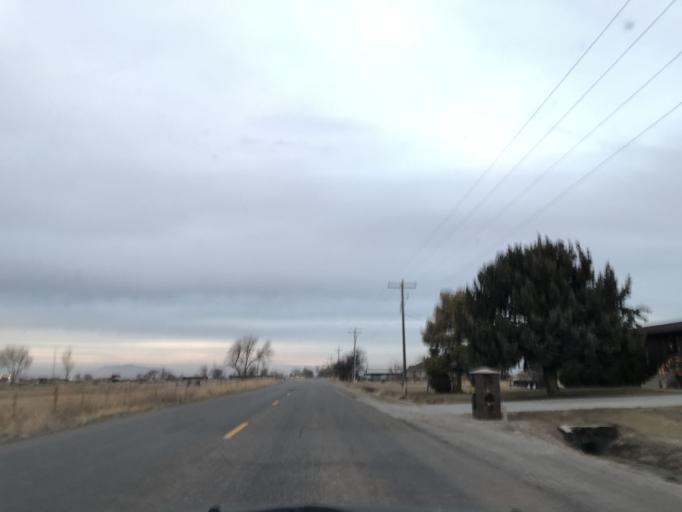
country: US
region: Utah
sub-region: Cache County
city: Benson
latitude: 41.7791
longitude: -111.9124
